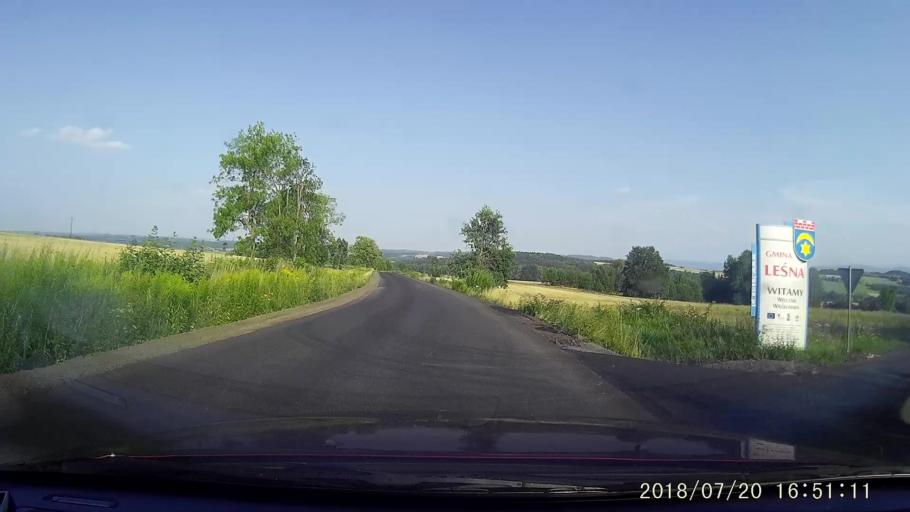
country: PL
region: Lower Silesian Voivodeship
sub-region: Powiat lubanski
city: Lesna
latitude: 51.0389
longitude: 15.2168
